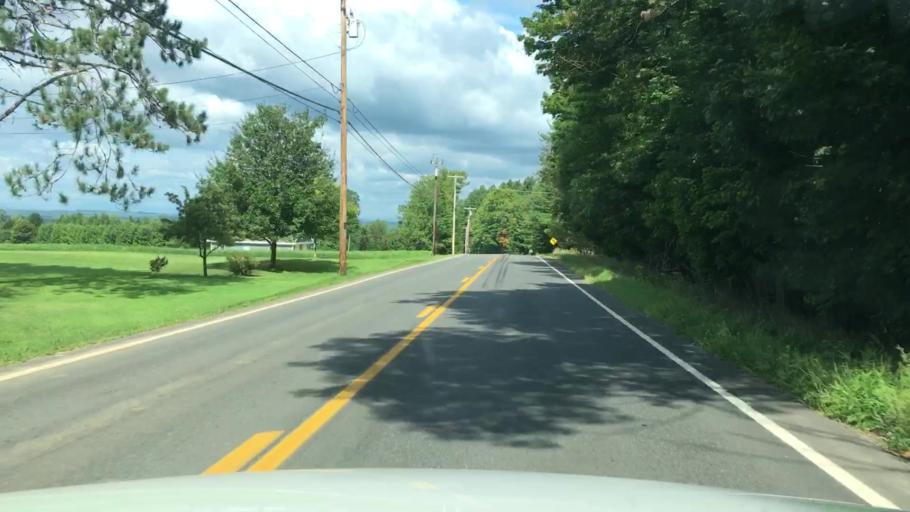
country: US
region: Maine
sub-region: Somerset County
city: Skowhegan
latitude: 44.7435
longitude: -69.6913
